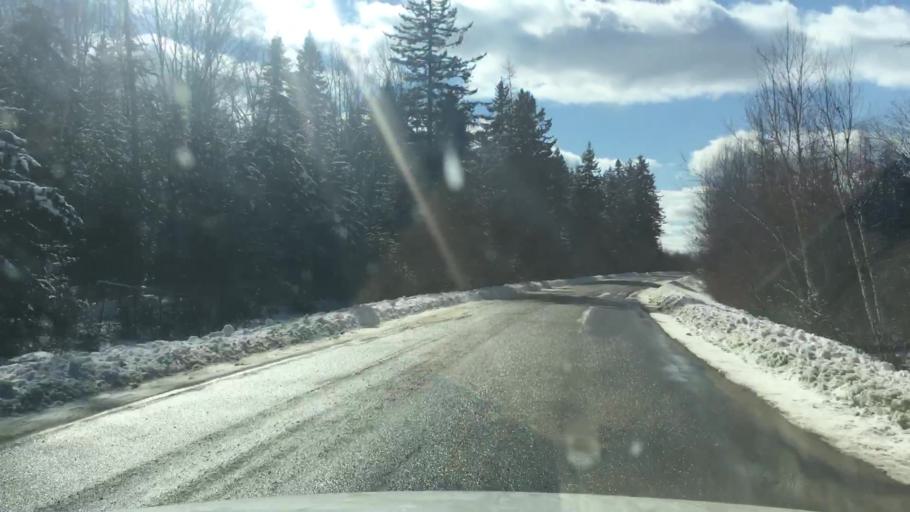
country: US
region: Maine
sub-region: Washington County
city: Machiasport
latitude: 44.6752
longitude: -67.4196
